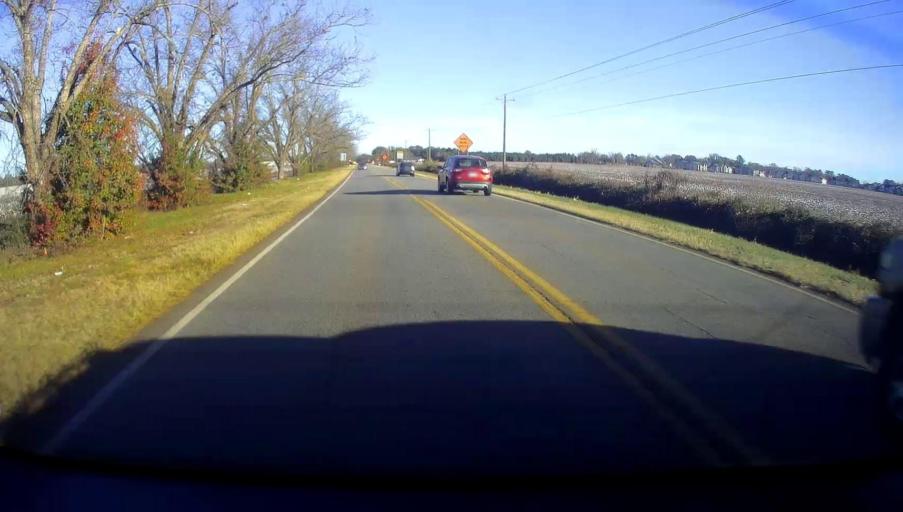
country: US
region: Georgia
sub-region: Houston County
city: Centerville
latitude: 32.5899
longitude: -83.7191
